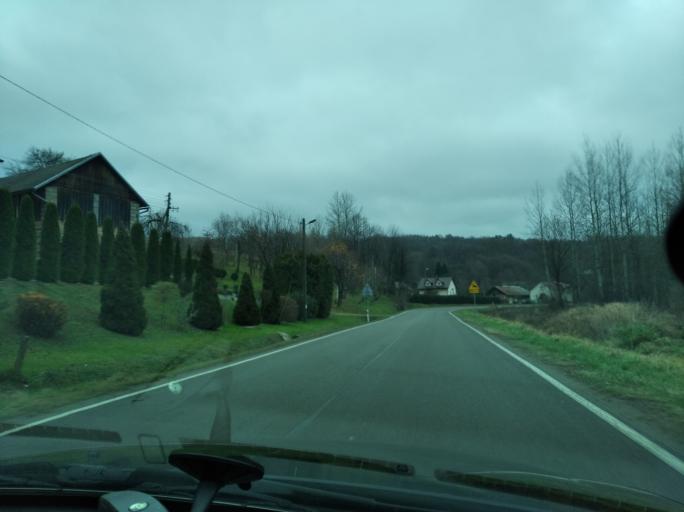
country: PL
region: Subcarpathian Voivodeship
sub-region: Powiat przeworski
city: Jawornik Polski
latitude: 49.9212
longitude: 22.3051
